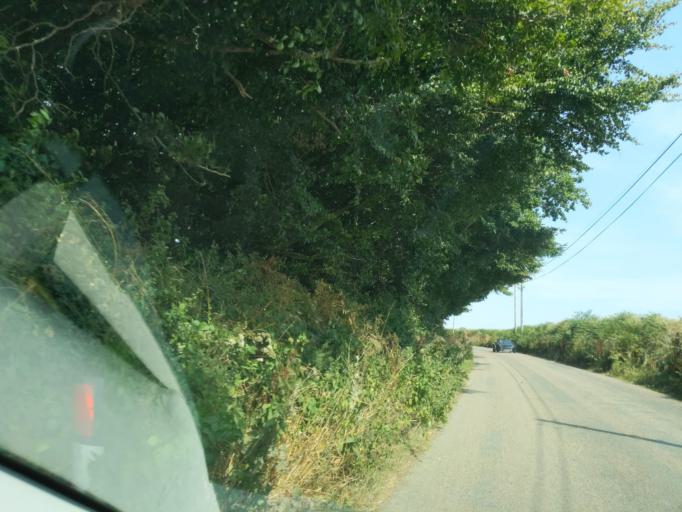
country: GB
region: England
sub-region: Devon
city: Winkleigh
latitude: 50.8559
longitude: -3.9234
